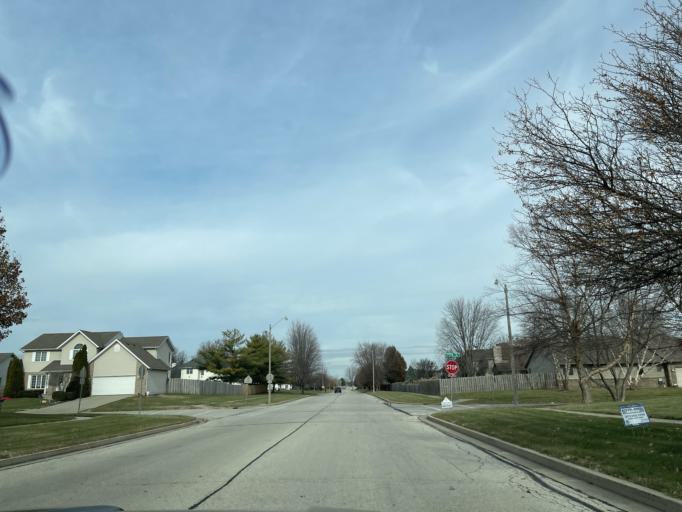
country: US
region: Illinois
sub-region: Sangamon County
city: Jerome
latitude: 39.7664
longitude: -89.7297
